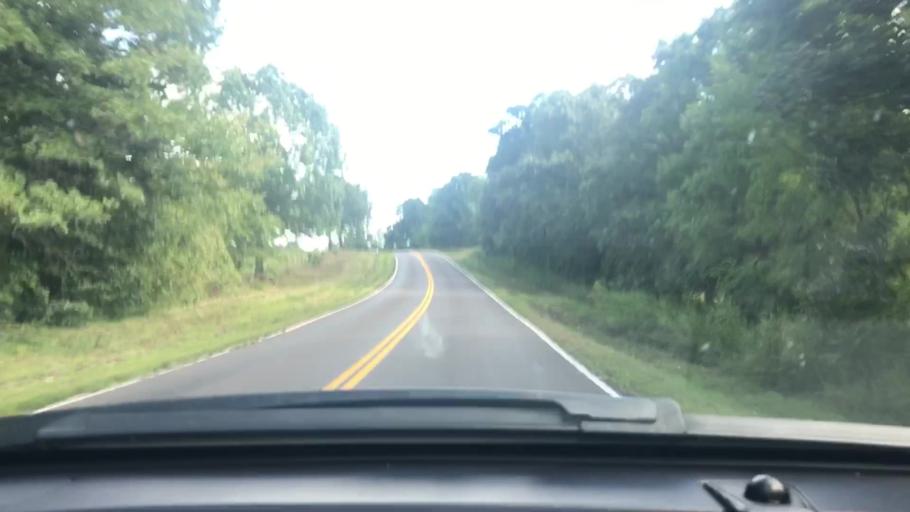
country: US
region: Missouri
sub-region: Wright County
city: Hartville
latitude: 37.3535
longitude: -92.3397
